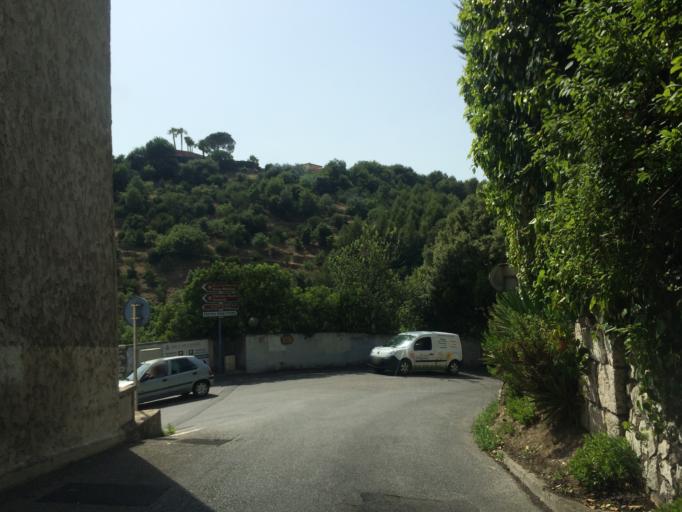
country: FR
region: Provence-Alpes-Cote d'Azur
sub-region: Departement des Alpes-Maritimes
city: Cagnes-sur-Mer
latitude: 43.6699
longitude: 7.1454
